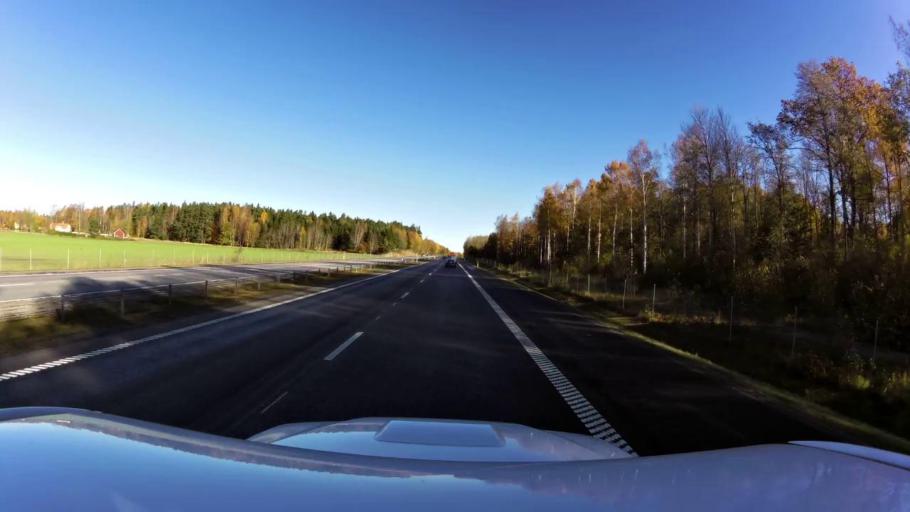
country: SE
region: OEstergoetland
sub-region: Linkopings Kommun
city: Malmslatt
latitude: 58.4184
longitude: 15.4805
